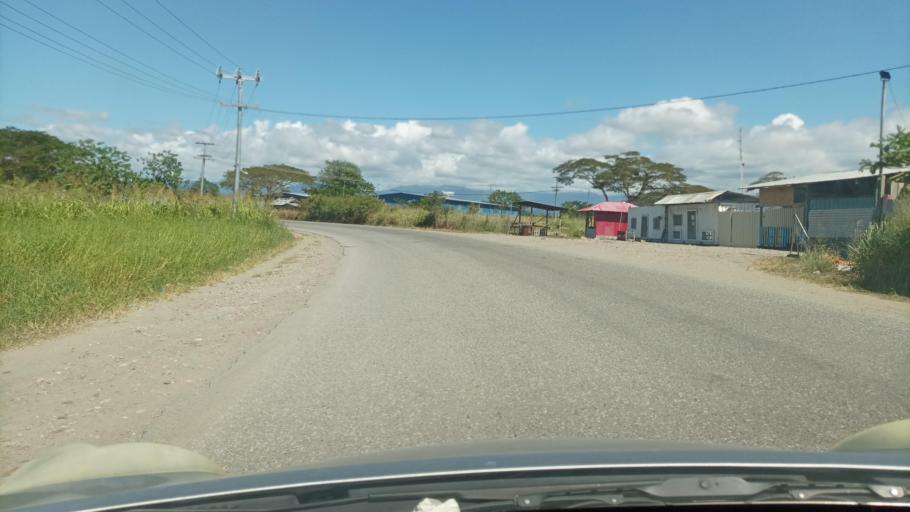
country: SB
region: Guadalcanal
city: Honiara
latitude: -9.4266
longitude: 160.0661
